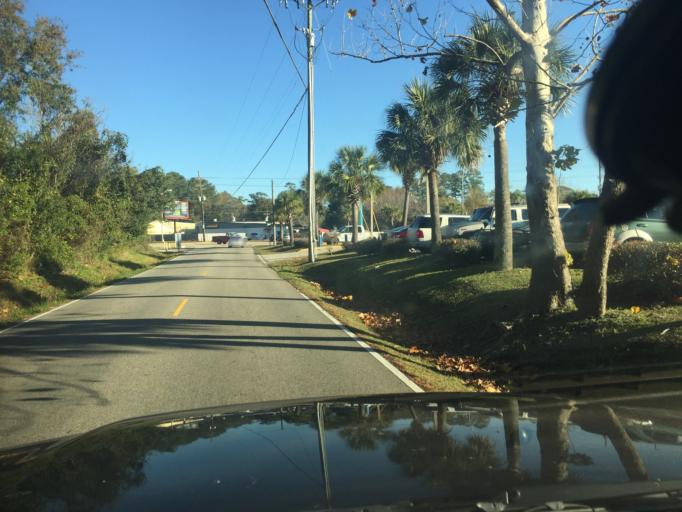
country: US
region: Louisiana
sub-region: Saint Tammany Parish
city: Slidell
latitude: 30.2512
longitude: -89.7681
